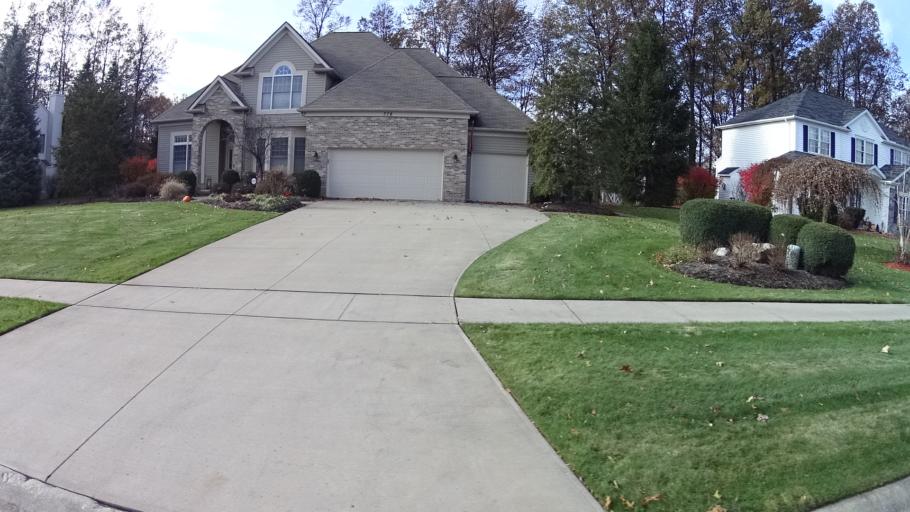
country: US
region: Ohio
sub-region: Lorain County
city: Avon Lake
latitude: 41.4981
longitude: -82.0293
